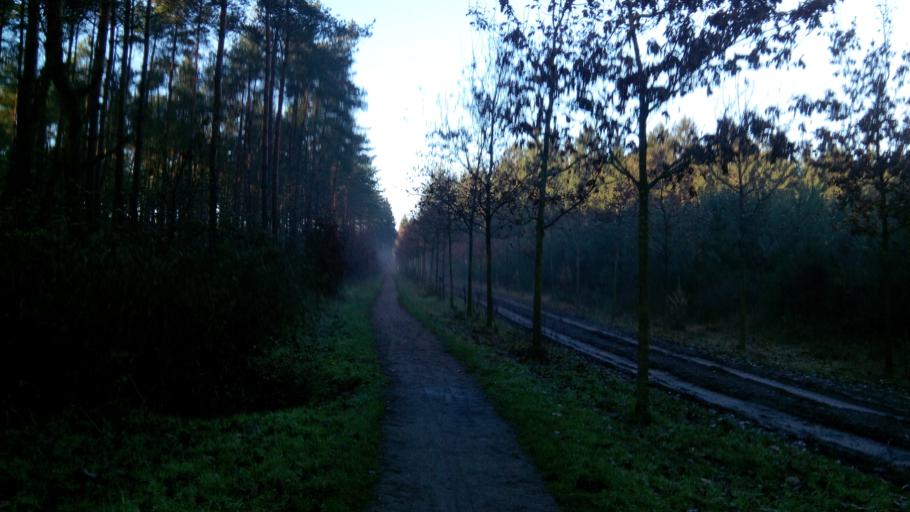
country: NL
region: Utrecht
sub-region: Gemeente Woudenberg
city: Woudenberg
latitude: 52.1085
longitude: 5.3852
